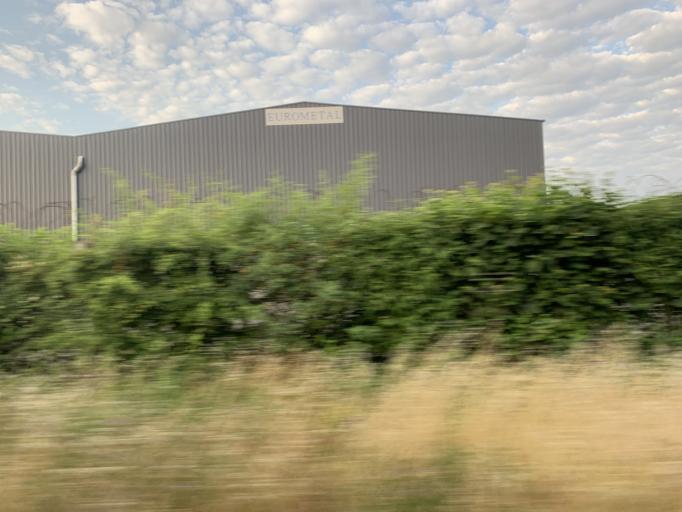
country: FR
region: Rhone-Alpes
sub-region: Departement du Rhone
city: Meyzieu
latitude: 45.7684
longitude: 5.0253
